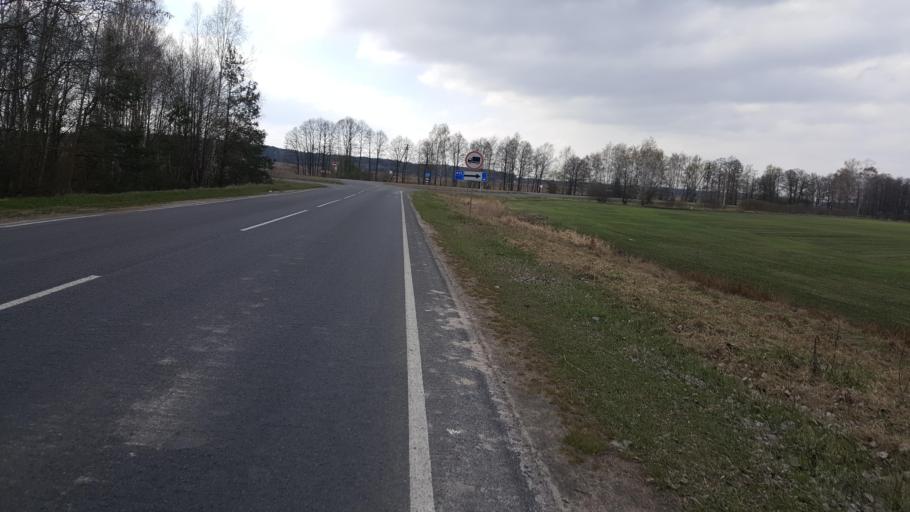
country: BY
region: Brest
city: Kamyanyets
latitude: 52.3440
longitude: 23.9073
